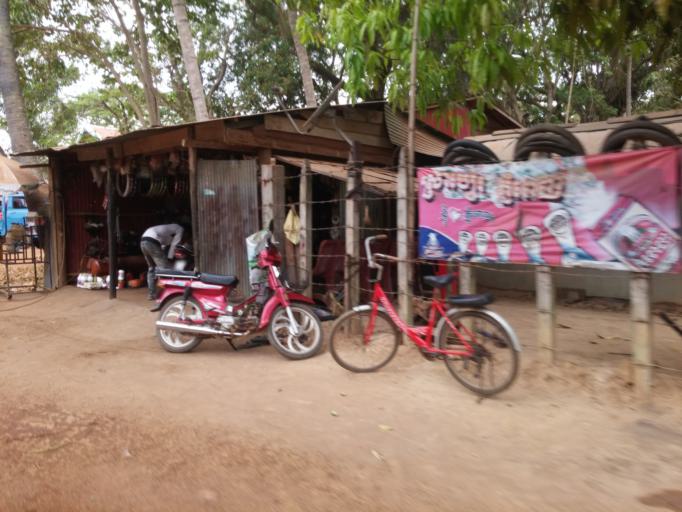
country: KH
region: Siem Reap
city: Siem Reap
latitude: 13.3257
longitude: 103.9955
